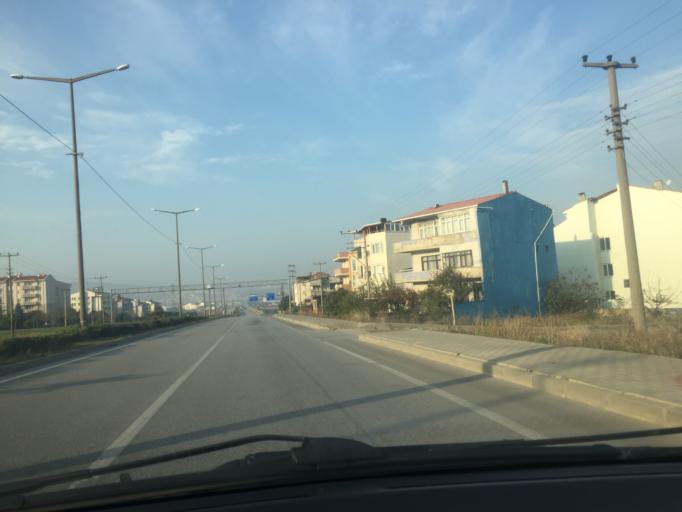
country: TR
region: Canakkale
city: Biga
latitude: 40.2426
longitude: 27.2652
